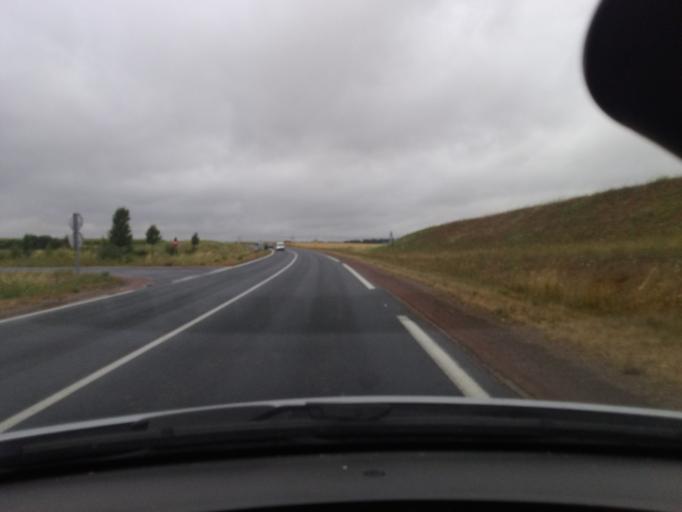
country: FR
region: Pays de la Loire
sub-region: Departement de la Vendee
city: Lucon
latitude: 46.4693
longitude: -1.1555
